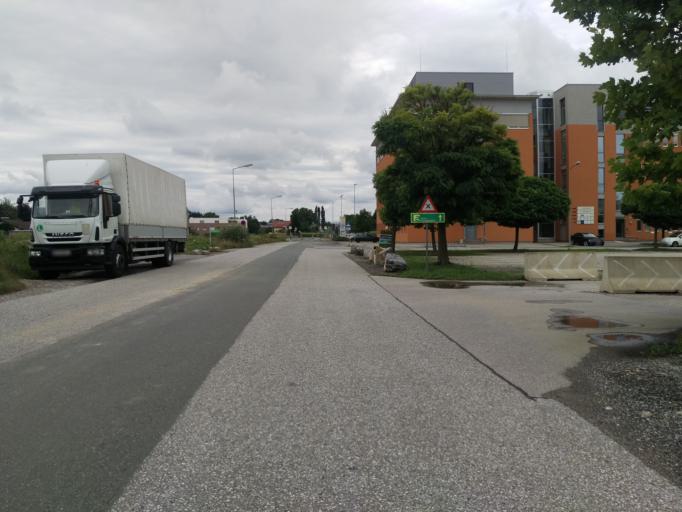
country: AT
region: Styria
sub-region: Politischer Bezirk Graz-Umgebung
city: Raaba
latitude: 47.0438
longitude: 15.4785
